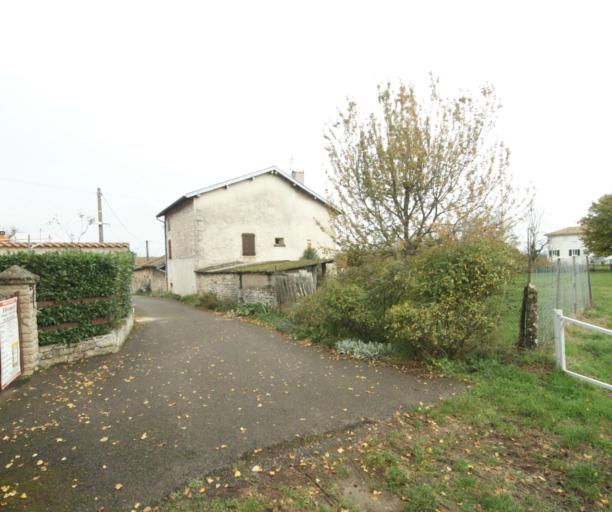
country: FR
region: Rhone-Alpes
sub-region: Departement de l'Ain
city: Pont-de-Vaux
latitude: 46.4702
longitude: 4.8849
